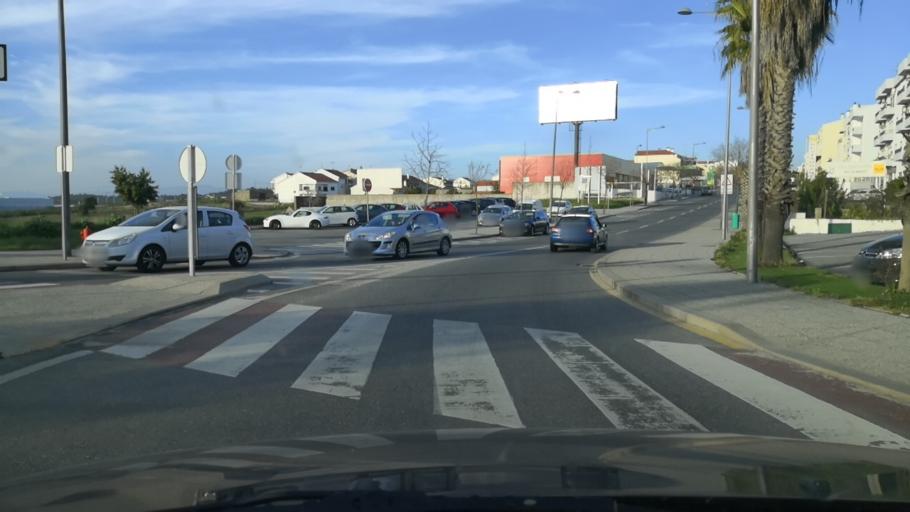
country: PT
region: Castelo Branco
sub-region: Castelo Branco
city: Castelo Branco
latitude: 39.8068
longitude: -7.5123
